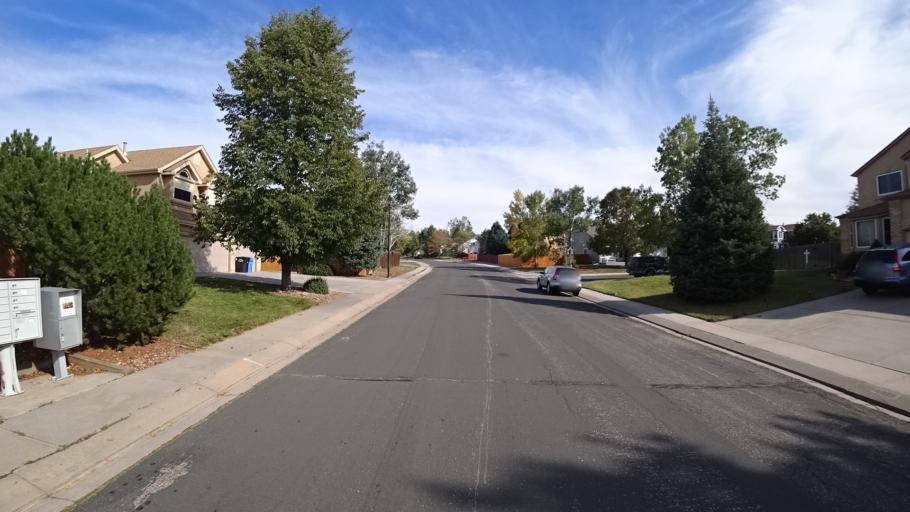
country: US
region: Colorado
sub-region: El Paso County
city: Cimarron Hills
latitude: 38.9047
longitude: -104.6937
